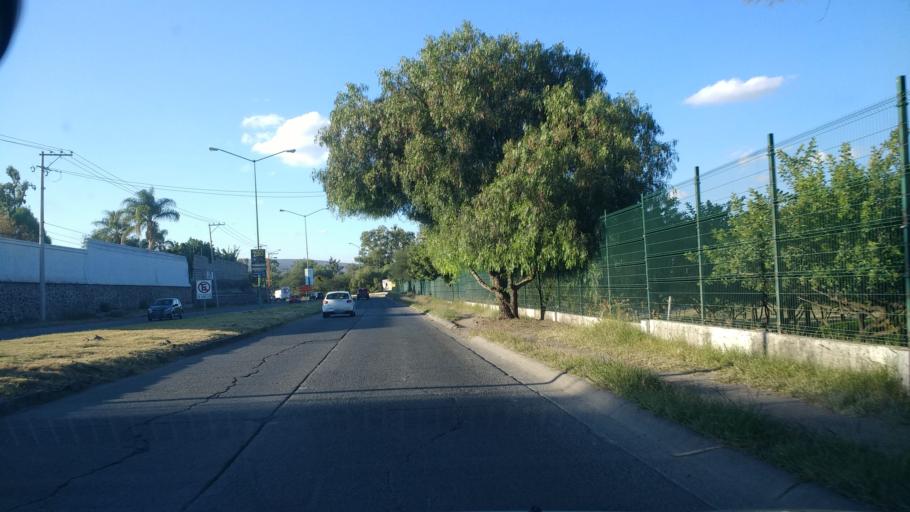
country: MX
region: Guanajuato
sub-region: Leon
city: La Ermita
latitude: 21.1752
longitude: -101.6990
